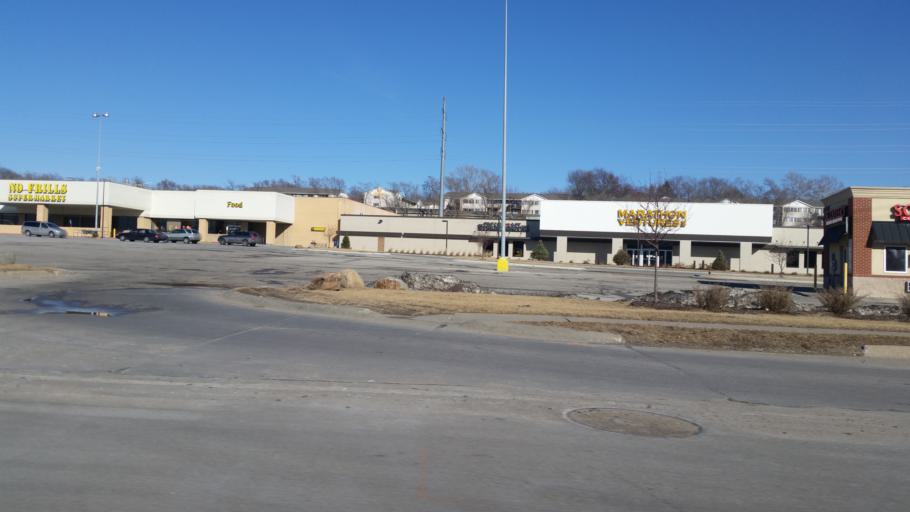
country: US
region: Nebraska
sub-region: Sarpy County
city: Bellevue
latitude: 41.1750
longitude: -95.9259
